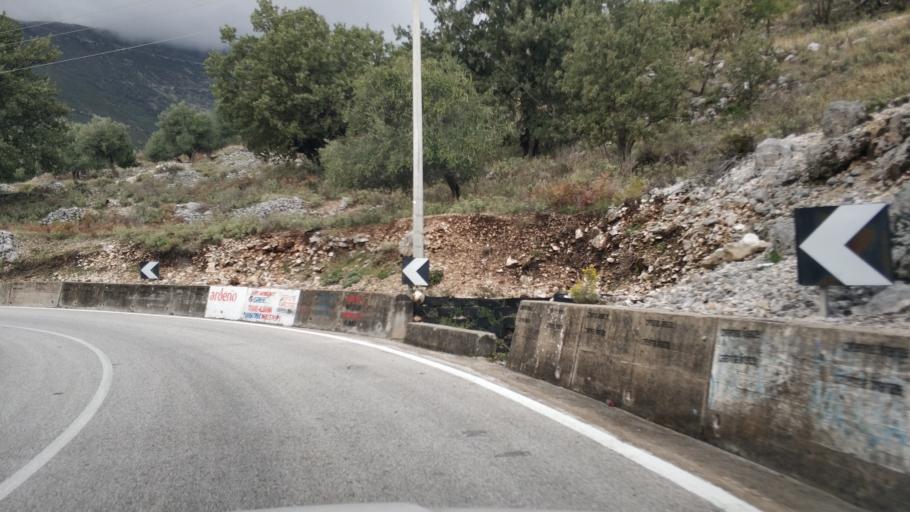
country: AL
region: Vlore
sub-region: Rrethi i Vlores
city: Vranisht
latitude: 40.1724
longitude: 19.6129
